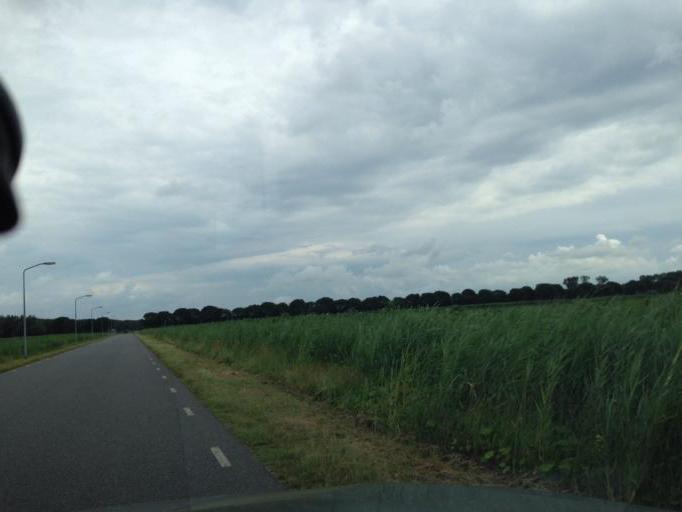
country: NL
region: Flevoland
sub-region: Gemeente Almere
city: Almere Stad
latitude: 52.3608
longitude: 5.2897
